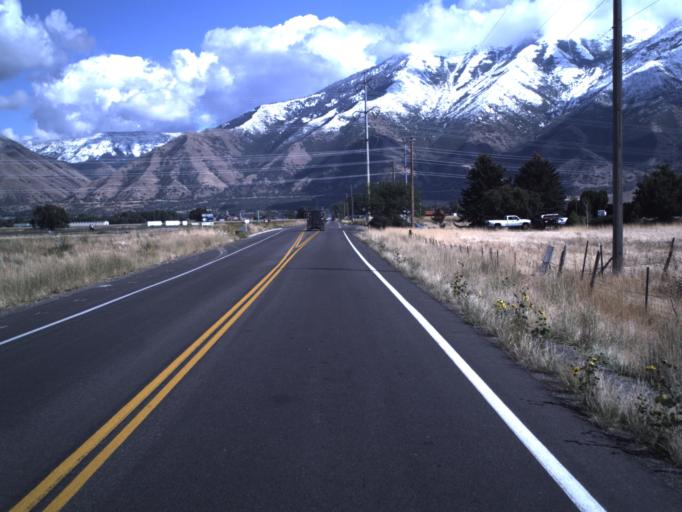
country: US
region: Utah
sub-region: Utah County
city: Mapleton
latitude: 40.1154
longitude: -111.6142
